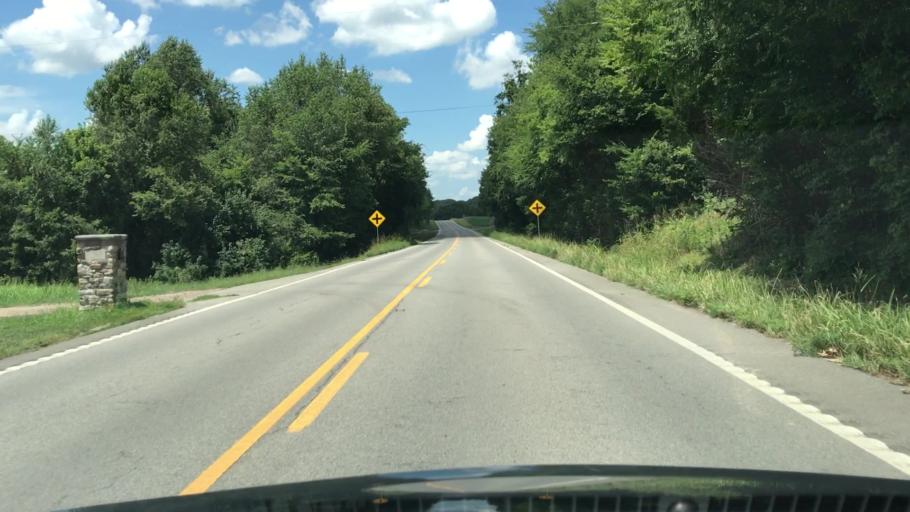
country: US
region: Tennessee
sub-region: Williamson County
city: Nolensville
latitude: 35.8524
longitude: -86.6334
